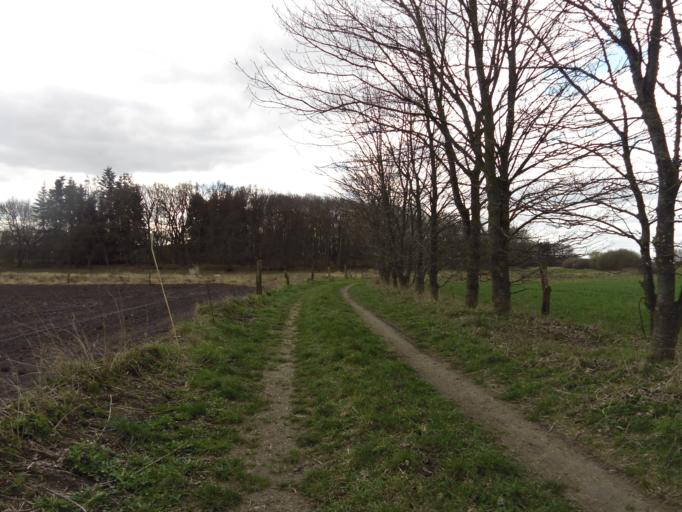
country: DK
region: South Denmark
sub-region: Tonder Kommune
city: Toftlund
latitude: 55.2334
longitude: 9.1393
